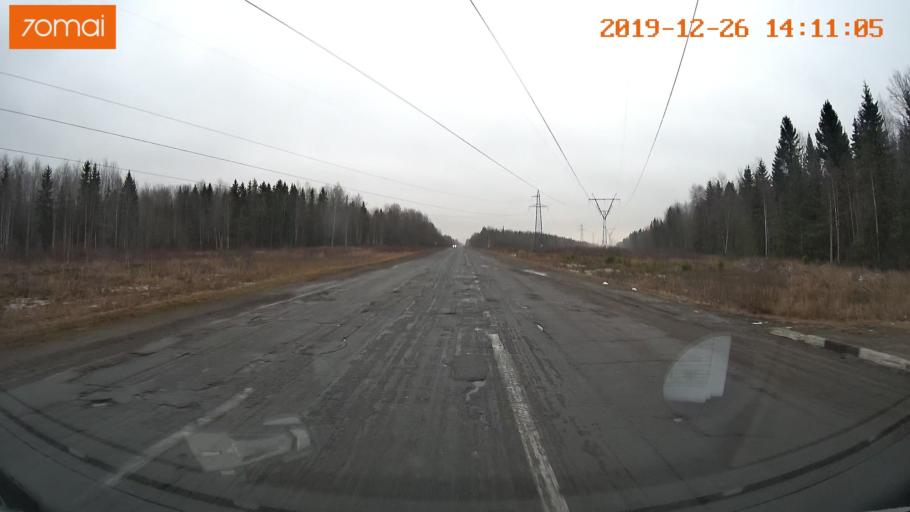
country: RU
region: Jaroslavl
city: Poshekhon'ye
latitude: 58.5091
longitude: 38.9666
